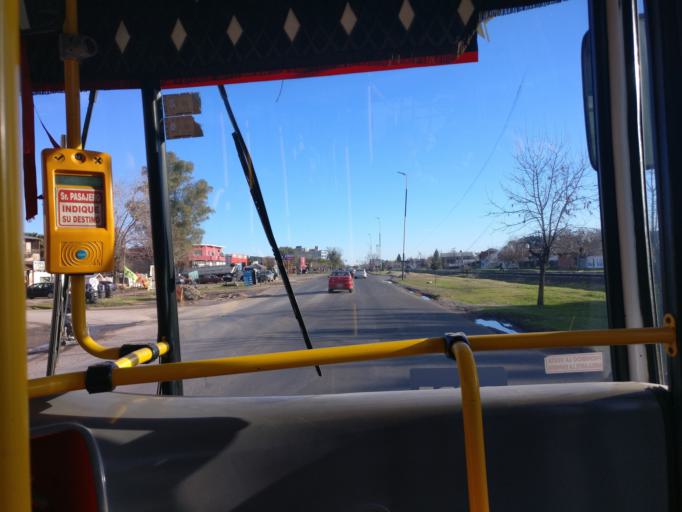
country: AR
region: Buenos Aires
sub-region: Partido de Ezeiza
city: Ezeiza
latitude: -34.8780
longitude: -58.5530
